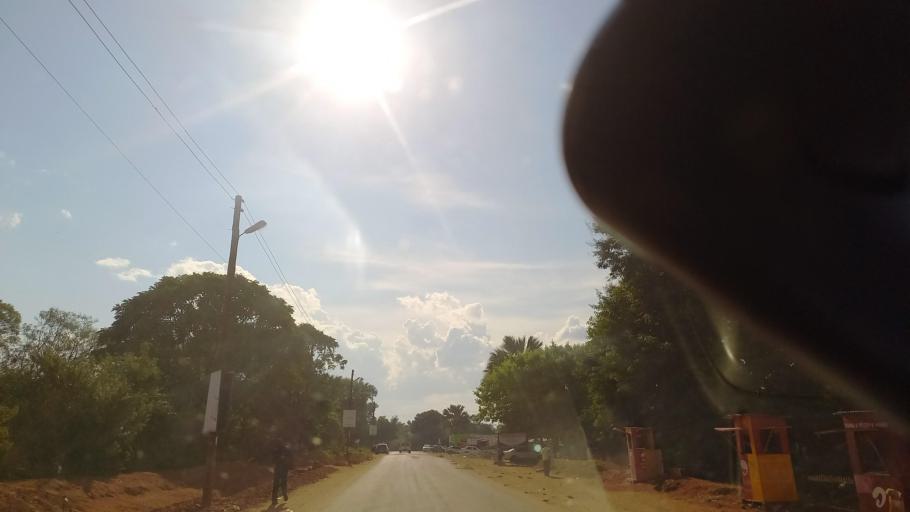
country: ZM
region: Southern
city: Mazabuka
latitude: -15.8611
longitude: 27.7624
